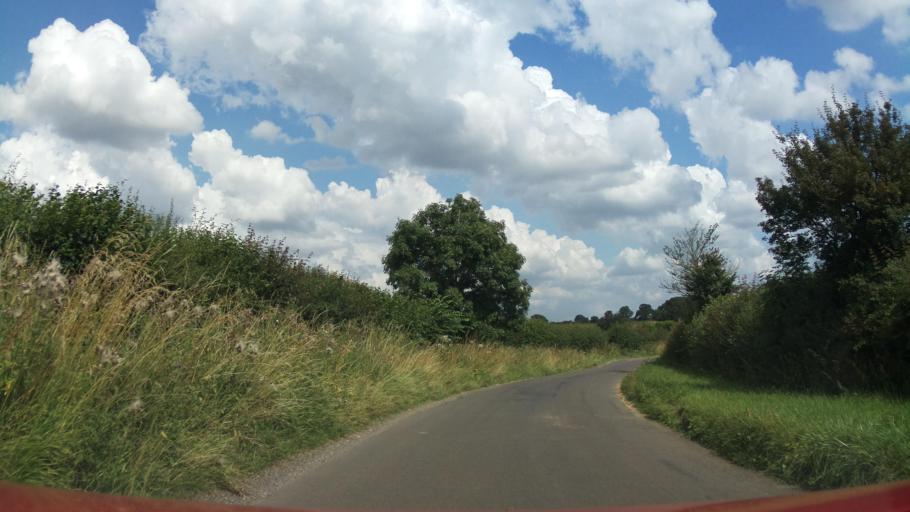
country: GB
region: England
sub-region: Wiltshire
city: Charlton
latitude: 51.6047
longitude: -2.0513
